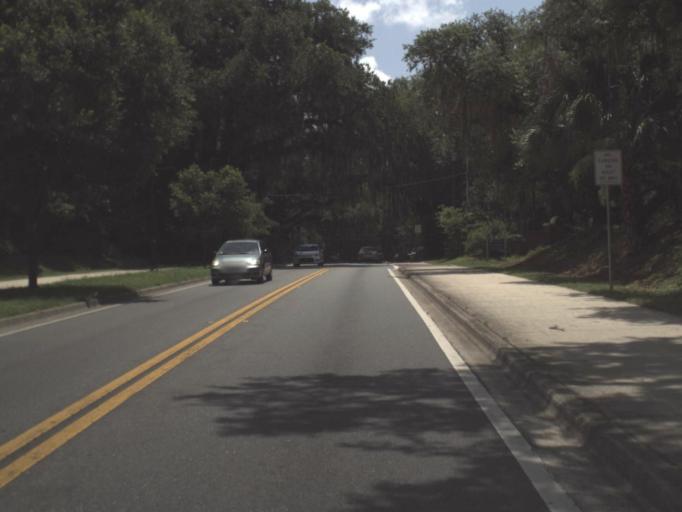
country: US
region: Florida
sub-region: Alachua County
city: Gainesville
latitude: 29.6504
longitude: -82.3648
